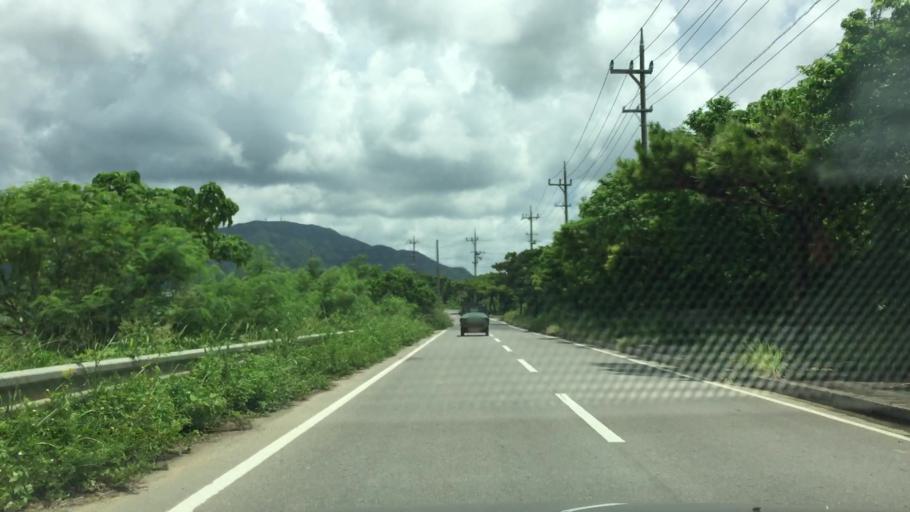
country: JP
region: Okinawa
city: Ishigaki
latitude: 24.3891
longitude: 124.1536
